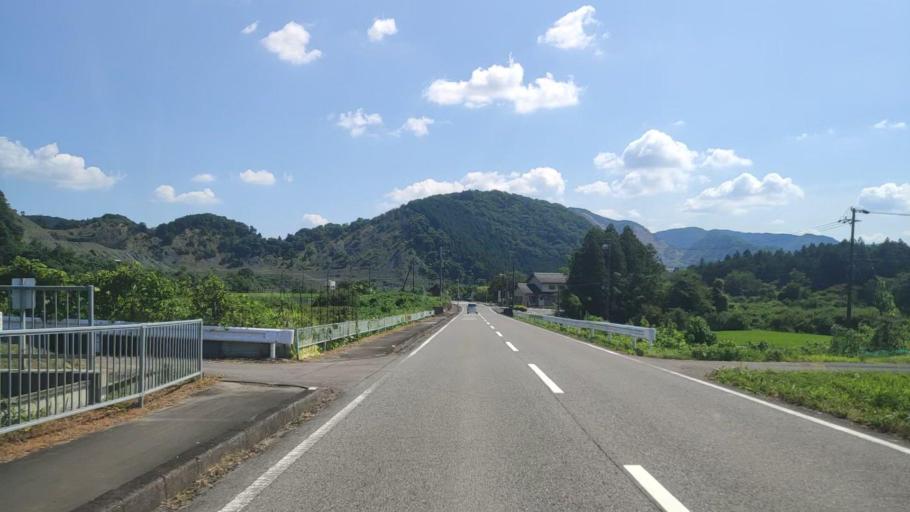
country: JP
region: Gifu
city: Godo
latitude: 35.5325
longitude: 136.6510
